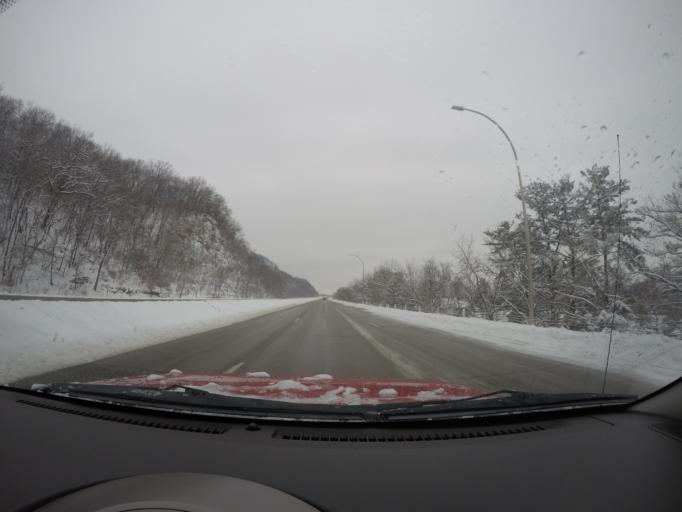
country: US
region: Wisconsin
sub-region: La Crosse County
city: Brice Prairie
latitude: 43.8938
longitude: -91.3440
